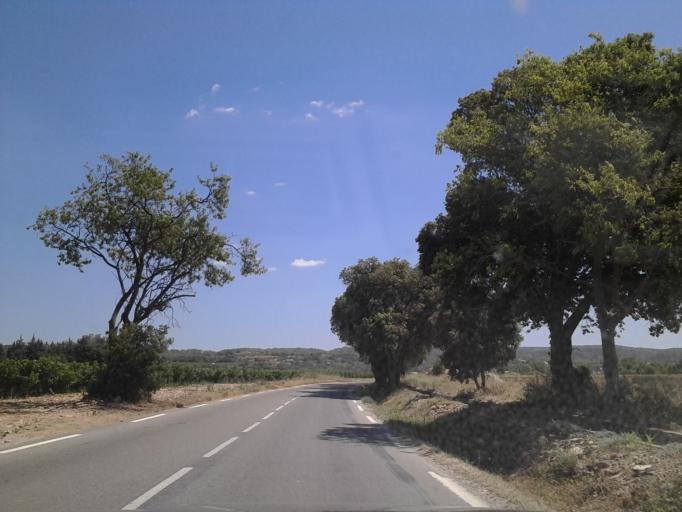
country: FR
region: Languedoc-Roussillon
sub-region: Departement de l'Herault
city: Aniane
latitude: 43.6991
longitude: 3.5742
